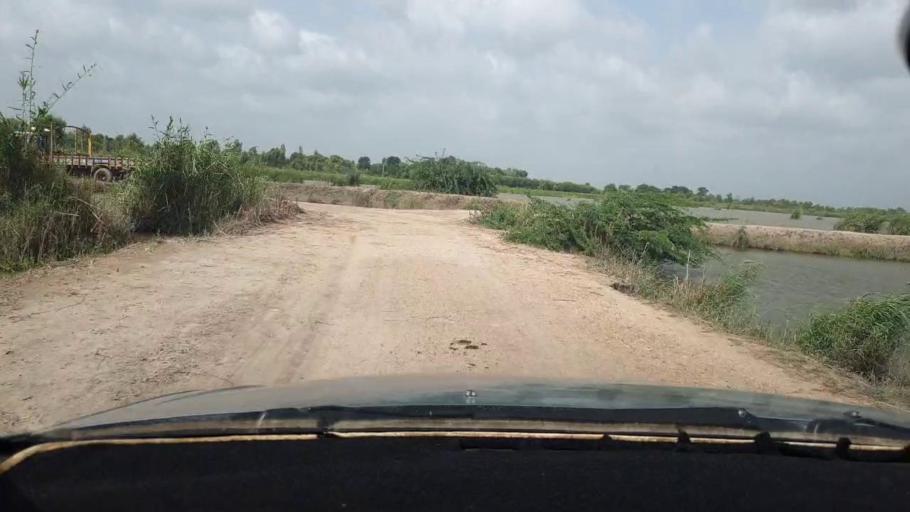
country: PK
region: Sindh
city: Tando Bago
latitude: 24.7747
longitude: 69.0201
